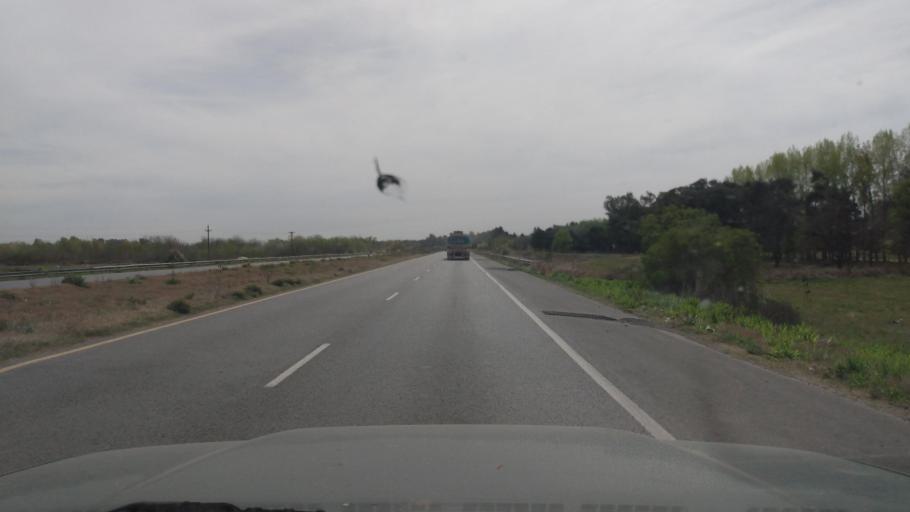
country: AR
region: Buenos Aires
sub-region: Partido de Lujan
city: Lujan
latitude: -34.5261
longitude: -59.0374
